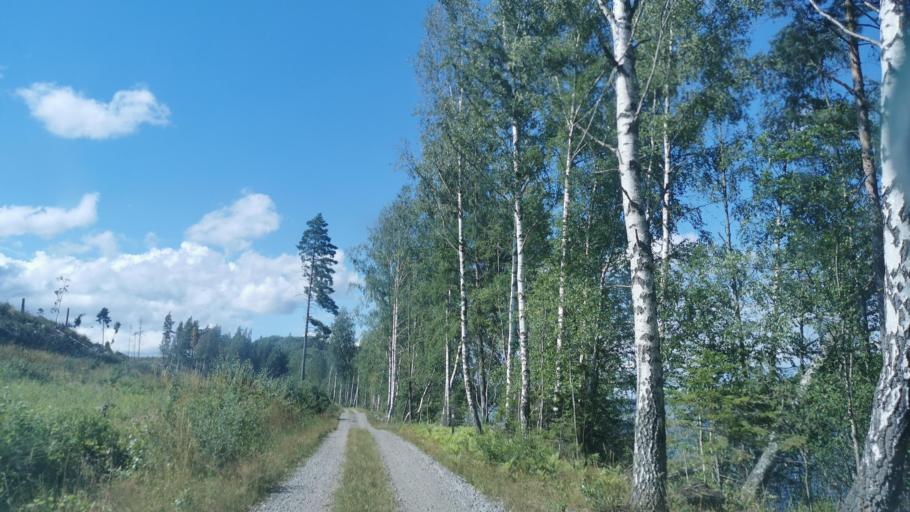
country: SE
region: OEstergoetland
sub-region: Finspangs Kommun
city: Finspang
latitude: 58.7936
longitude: 15.8284
